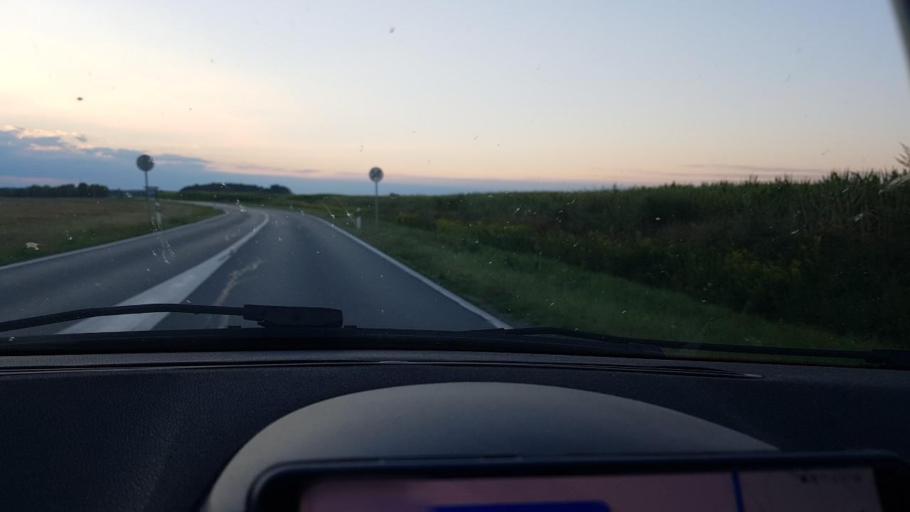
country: HR
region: Bjelovarsko-Bilogorska
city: Zdralovi
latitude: 45.8454
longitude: 16.9463
